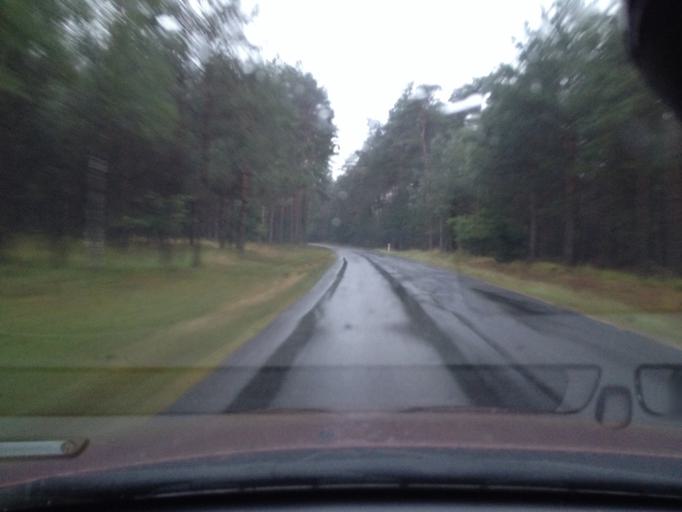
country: PL
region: Lubusz
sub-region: Powiat zaganski
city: Gozdnica
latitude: 51.3426
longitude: 15.1097
